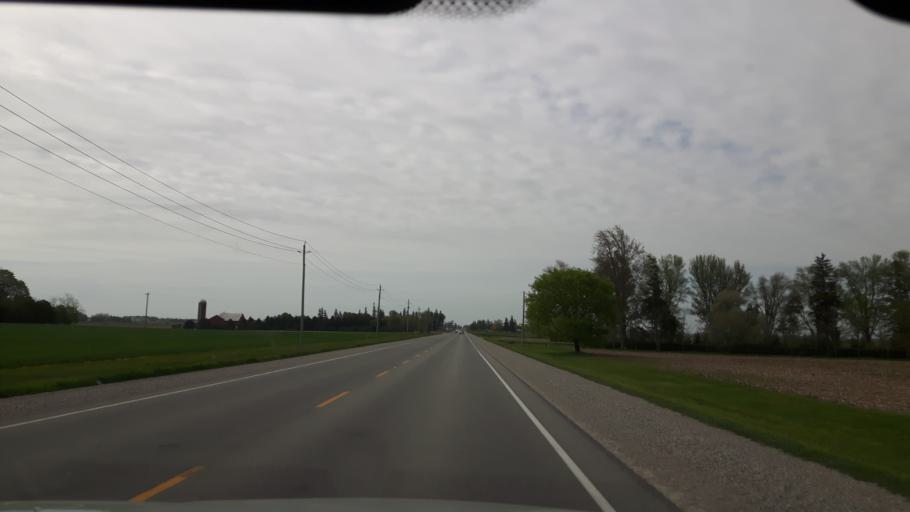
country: CA
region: Ontario
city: South Huron
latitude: 43.3835
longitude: -81.4881
